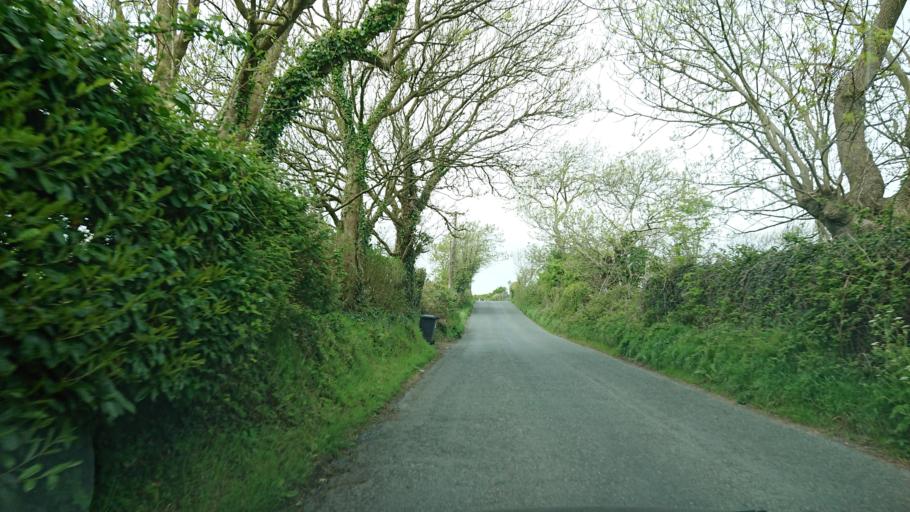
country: IE
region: Munster
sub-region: Waterford
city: Waterford
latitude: 52.2066
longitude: -7.0965
